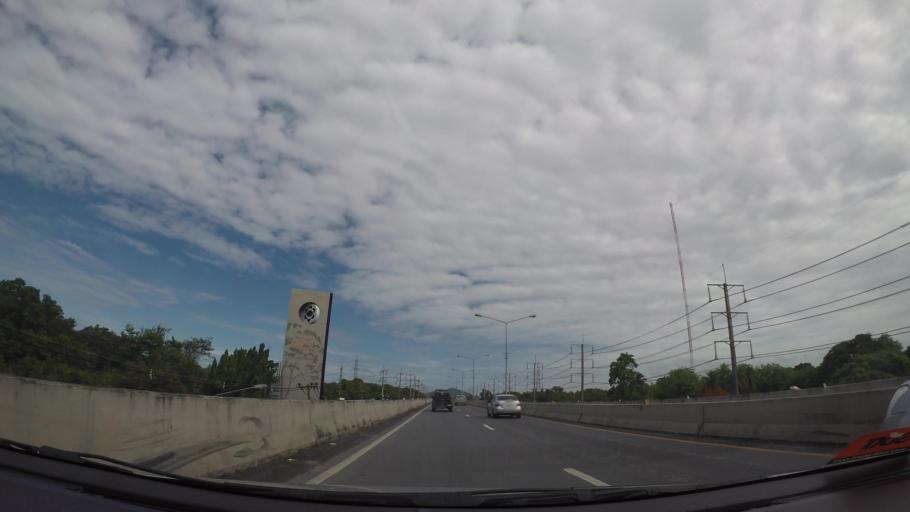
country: TH
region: Rayong
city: Ban Chang
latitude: 12.7278
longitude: 101.1435
